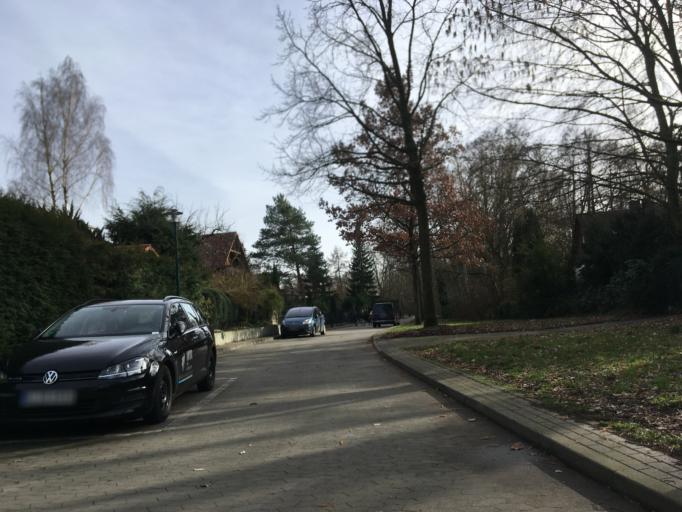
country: DE
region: Berlin
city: Lubars
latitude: 52.6134
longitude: 13.3522
